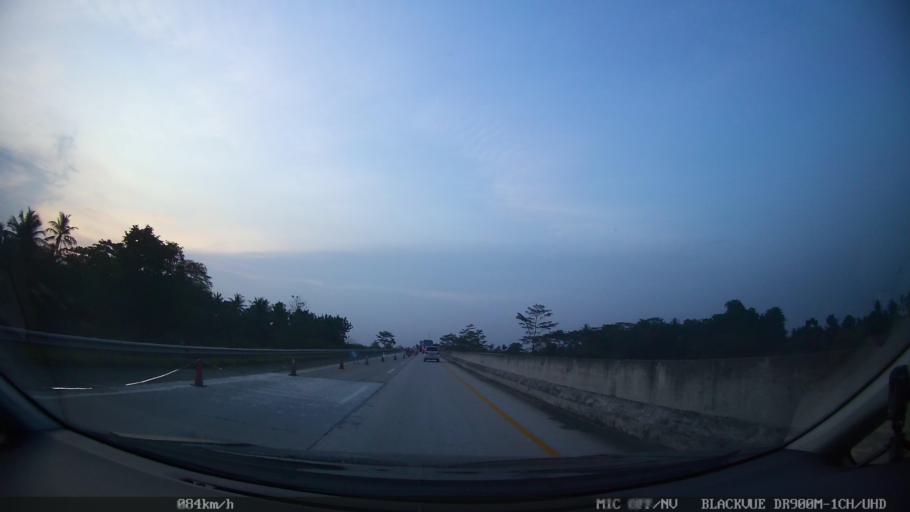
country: ID
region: Lampung
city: Kalianda
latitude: -5.6716
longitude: 105.6019
